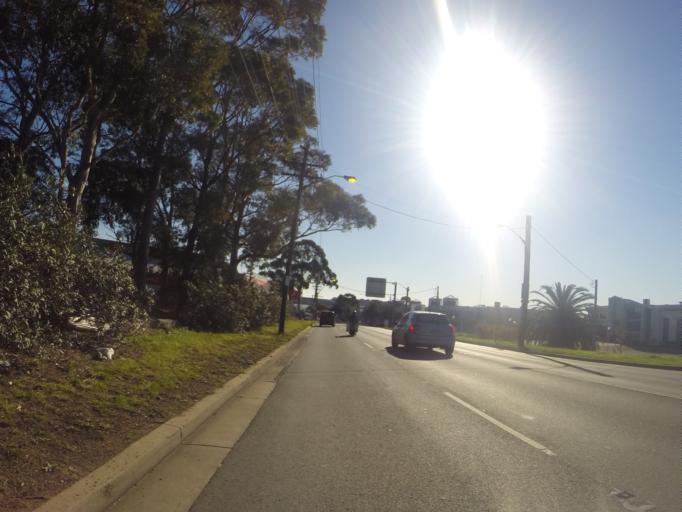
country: AU
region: New South Wales
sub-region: Bankstown
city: Bankstown
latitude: -33.9006
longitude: 151.0446
